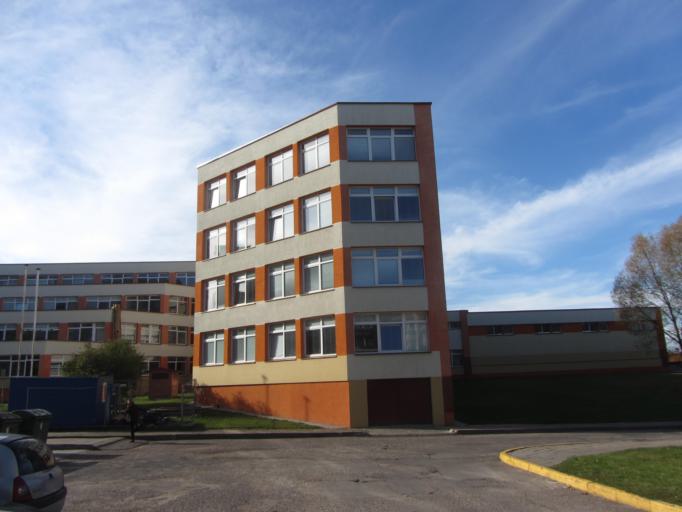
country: LT
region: Vilnius County
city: Elektrenai
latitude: 54.7870
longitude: 24.6795
